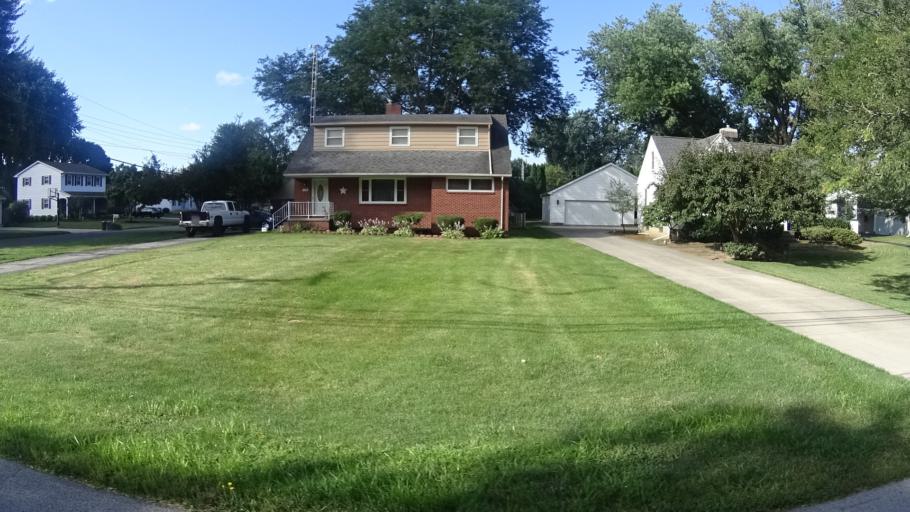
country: US
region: Ohio
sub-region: Erie County
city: Sandusky
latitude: 41.4320
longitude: -82.6770
